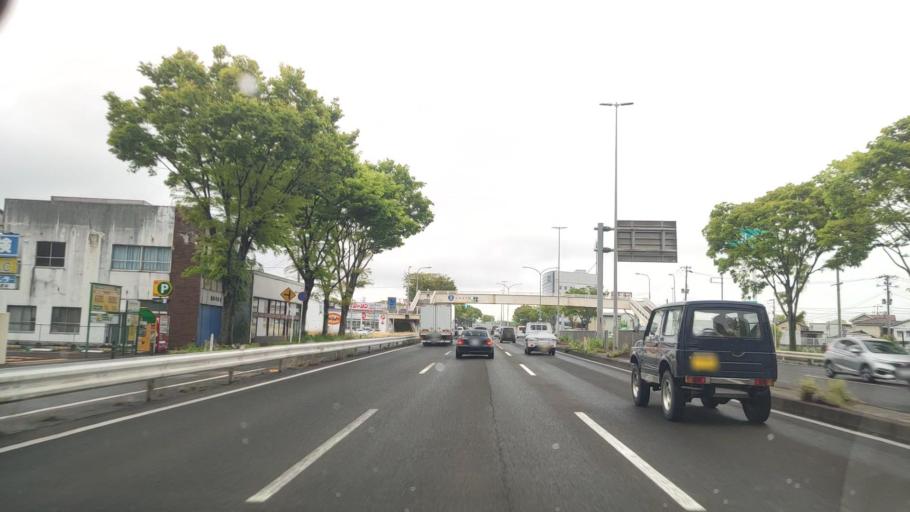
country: JP
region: Miyagi
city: Sendai
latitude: 38.2294
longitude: 140.9051
